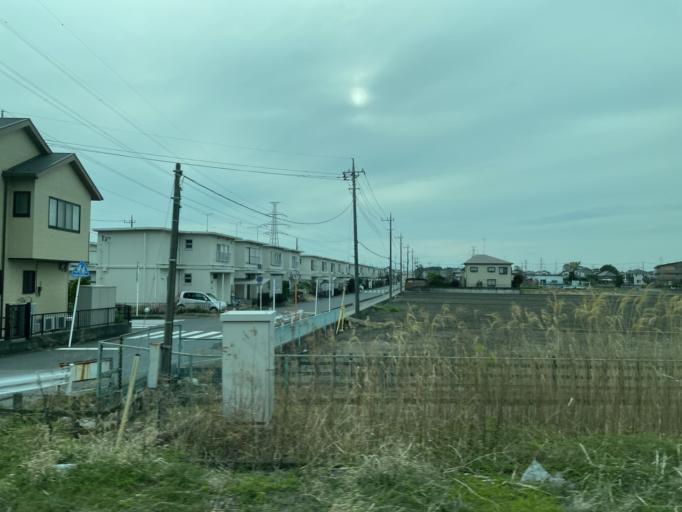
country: JP
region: Saitama
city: Kasukabe
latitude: 36.0067
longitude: 139.7378
